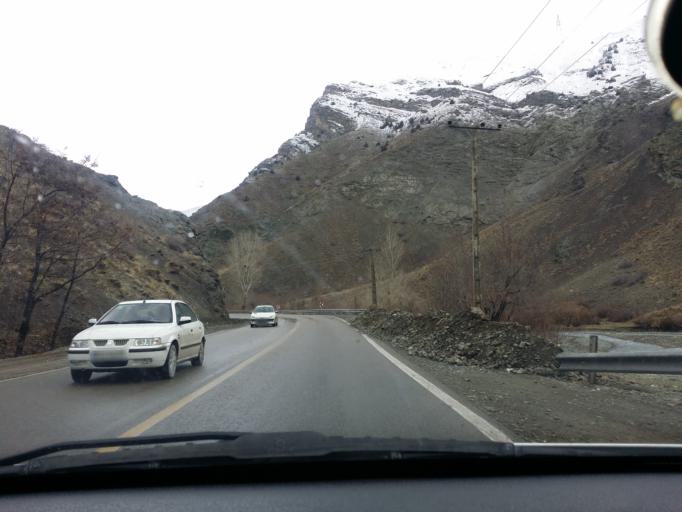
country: IR
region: Tehran
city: Tajrish
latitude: 36.0158
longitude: 51.2806
